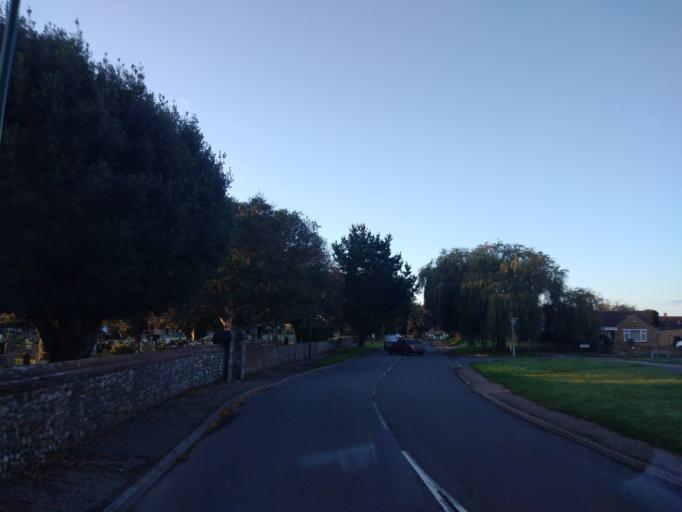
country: GB
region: England
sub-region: West Sussex
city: Littlehampton
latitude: 50.8185
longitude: -0.5285
